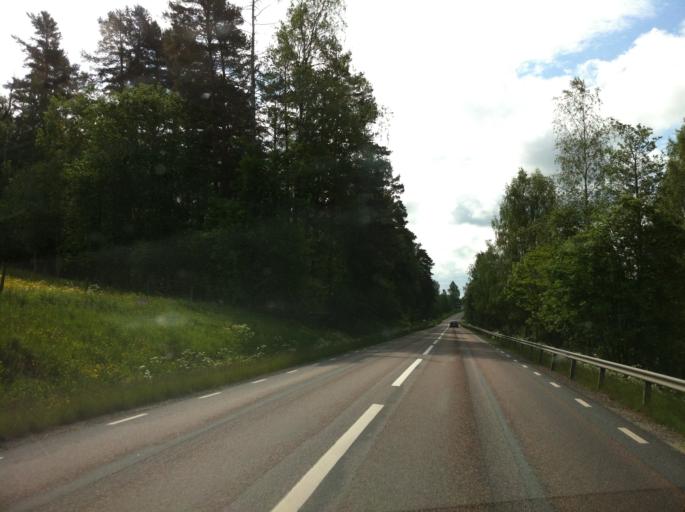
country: SE
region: Vaermland
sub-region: Sunne Kommun
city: Sunne
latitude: 59.6357
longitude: 13.1572
